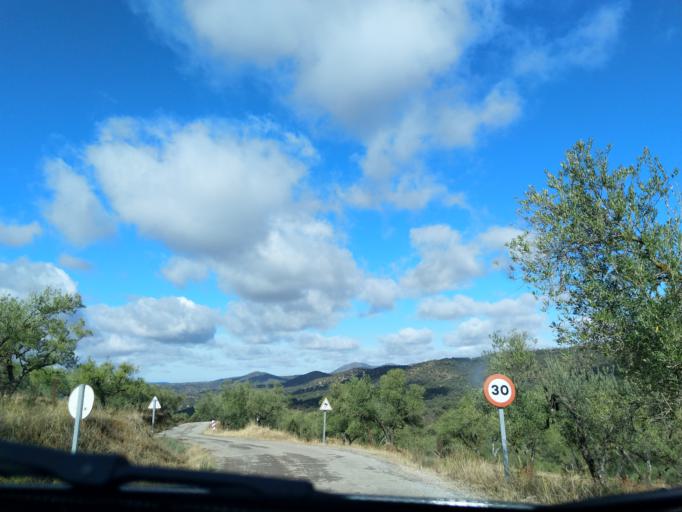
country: ES
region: Extremadura
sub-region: Provincia de Badajoz
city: Reina
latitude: 38.1283
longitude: -5.9238
